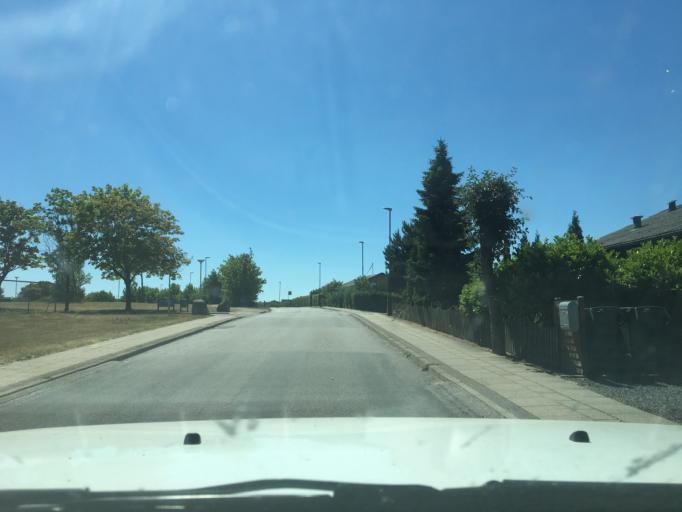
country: DK
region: Central Jutland
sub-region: Syddjurs Kommune
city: Hornslet
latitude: 56.3342
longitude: 10.3754
